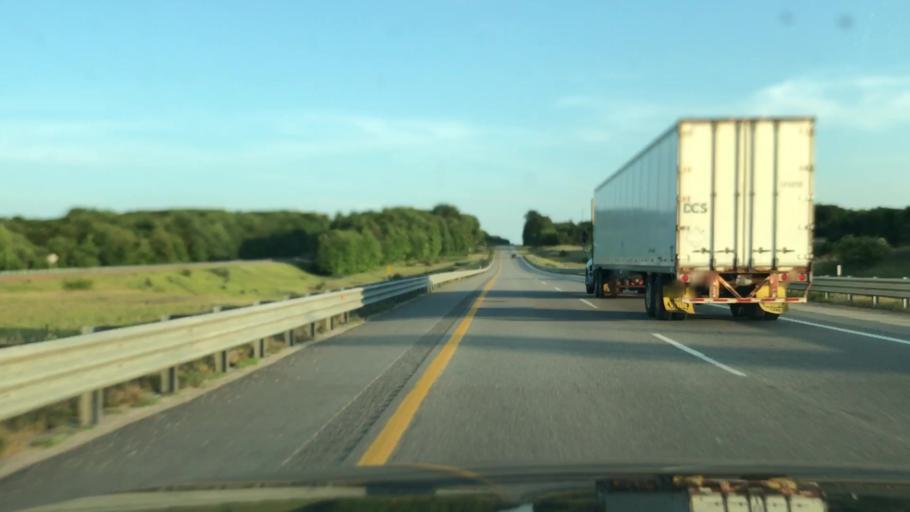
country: US
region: Michigan
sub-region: Osceola County
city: Reed City
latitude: 43.8585
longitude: -85.5349
